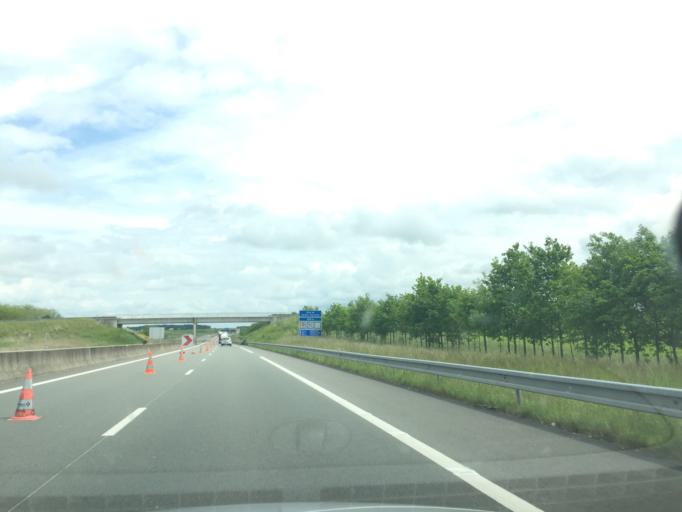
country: FR
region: Centre
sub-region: Departement d'Indre-et-Loire
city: Saint-Christophe-sur-le-Nais
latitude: 47.6514
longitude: 0.4559
